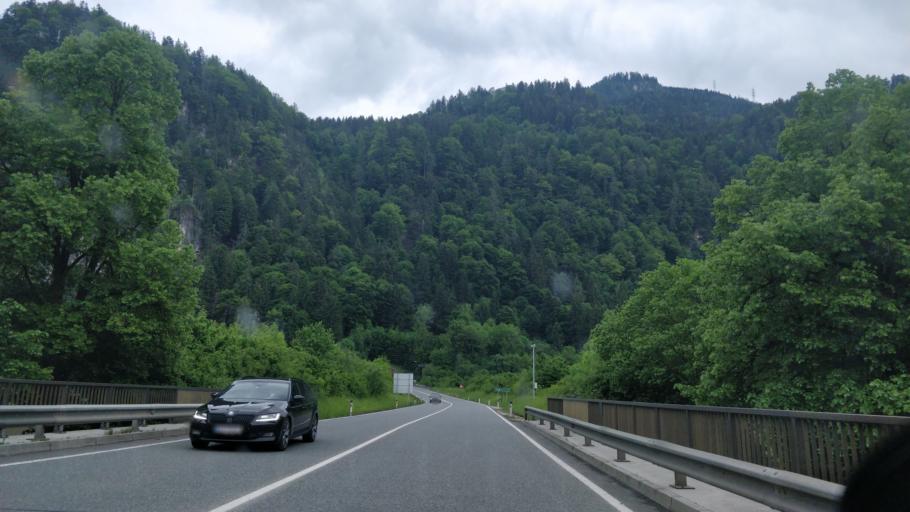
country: AT
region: Tyrol
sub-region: Politischer Bezirk Schwaz
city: Strass im Zillertal
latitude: 47.3957
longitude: 11.8096
